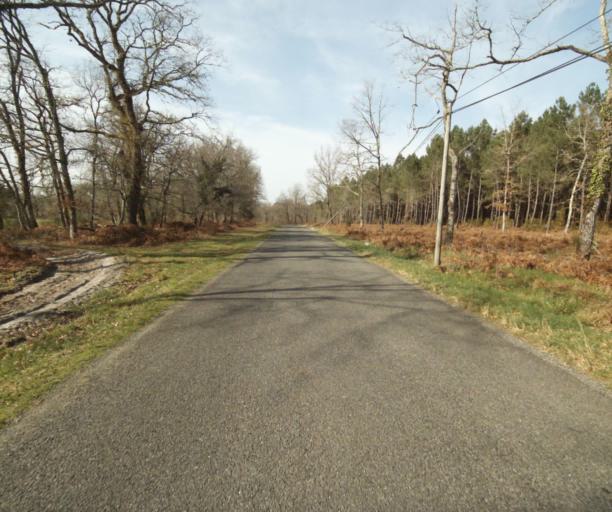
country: FR
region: Aquitaine
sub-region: Departement des Landes
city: Roquefort
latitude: 44.1252
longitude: -0.2052
